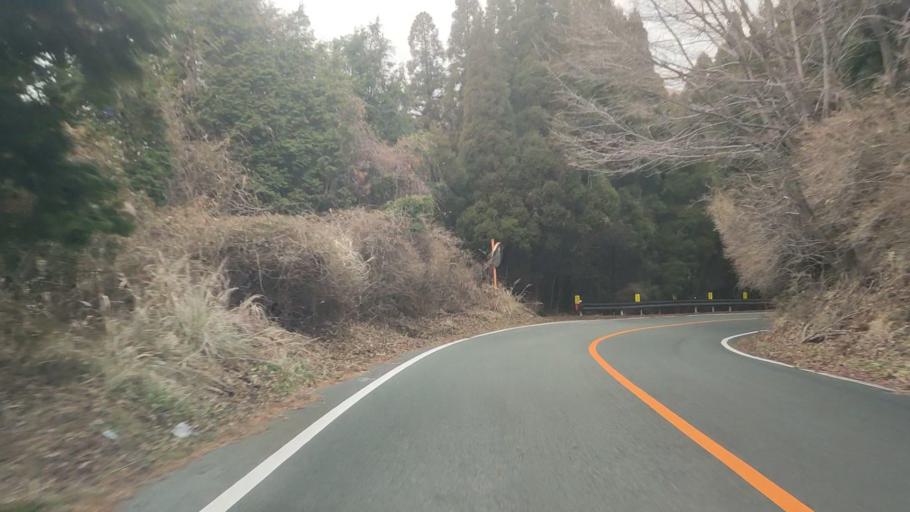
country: JP
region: Kumamoto
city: Aso
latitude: 32.9063
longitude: 131.1443
